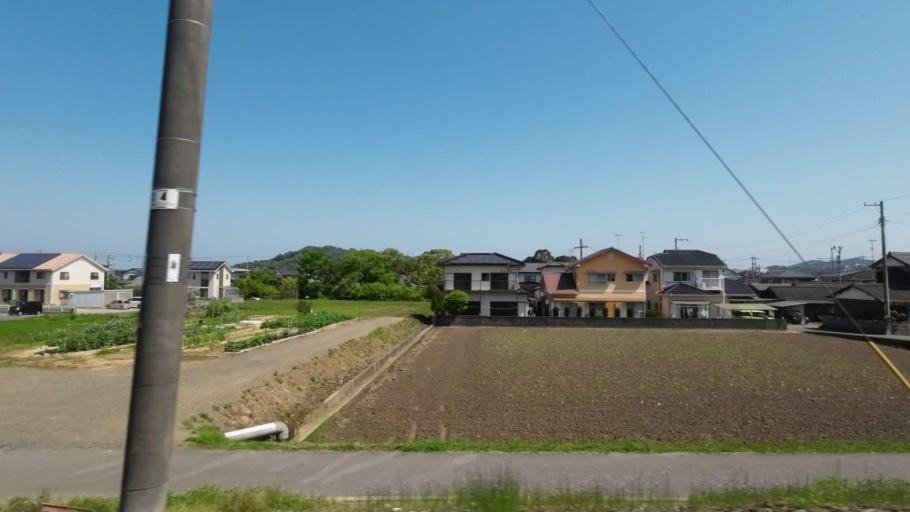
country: JP
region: Ehime
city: Niihama
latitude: 33.9706
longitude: 133.3275
